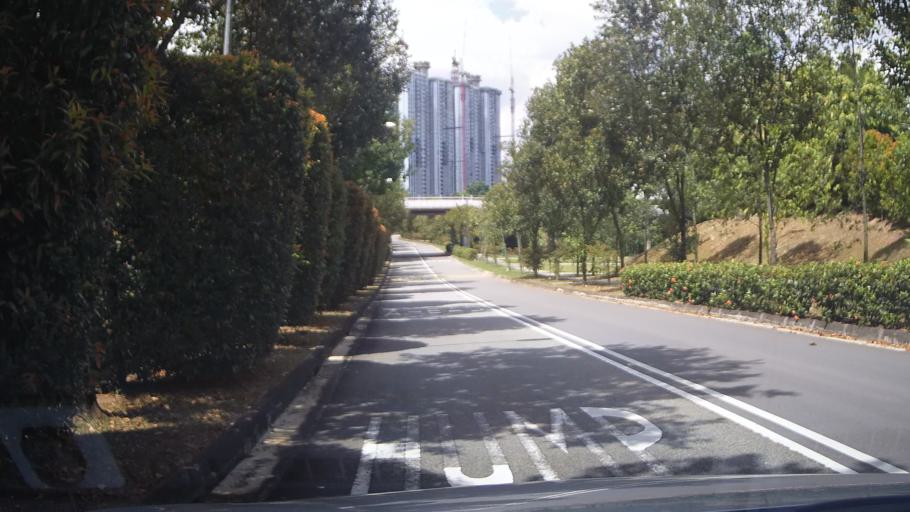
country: SG
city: Singapore
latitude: 1.3223
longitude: 103.7584
